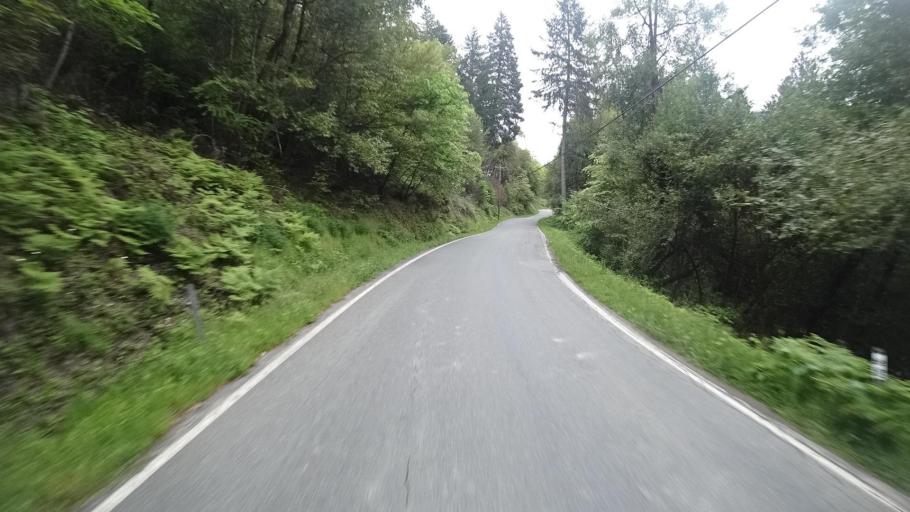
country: US
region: California
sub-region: Humboldt County
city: Willow Creek
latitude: 41.1999
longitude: -123.7464
